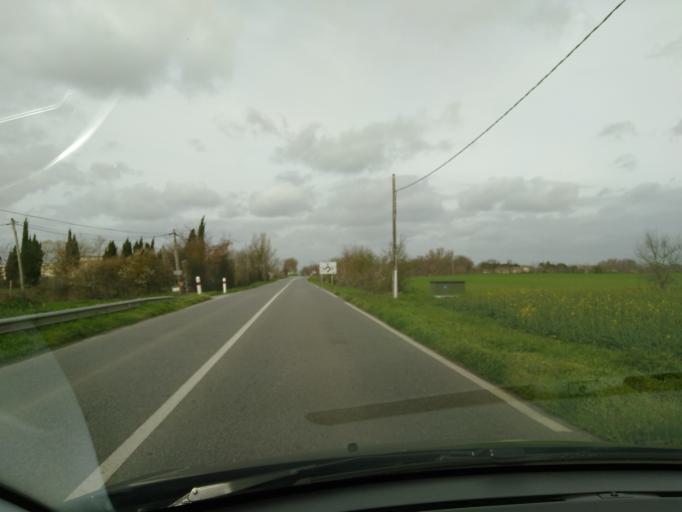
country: FR
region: Midi-Pyrenees
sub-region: Departement de la Haute-Garonne
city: Seilh
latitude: 43.7171
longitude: 1.3330
